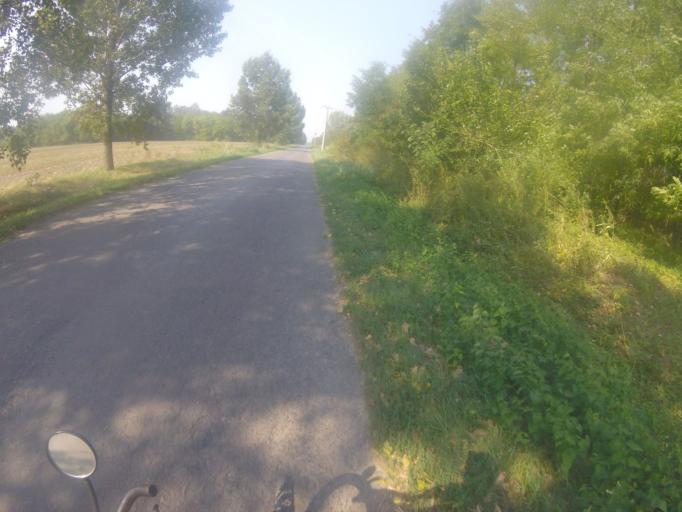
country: HU
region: Bacs-Kiskun
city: Ersekcsanad
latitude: 46.2540
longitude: 18.9650
